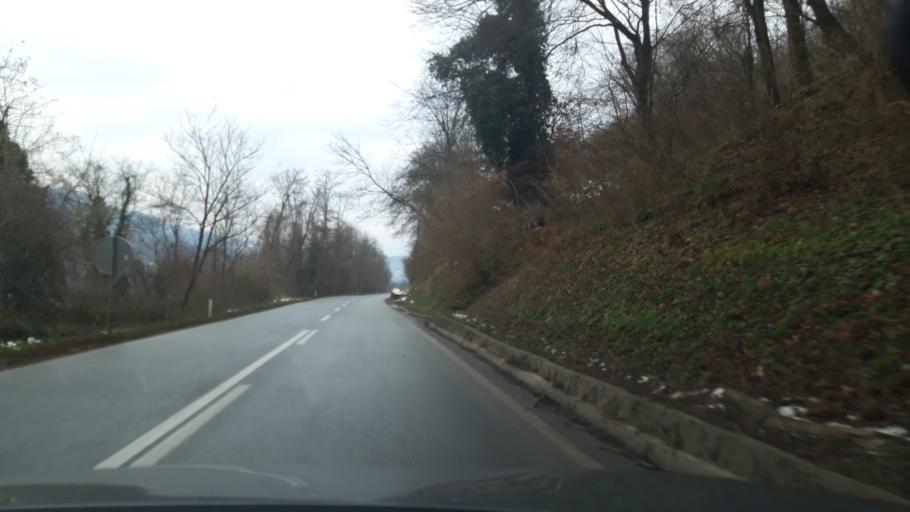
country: RS
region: Central Serbia
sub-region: Macvanski Okrug
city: Mali Zvornik
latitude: 44.3045
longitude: 19.1401
